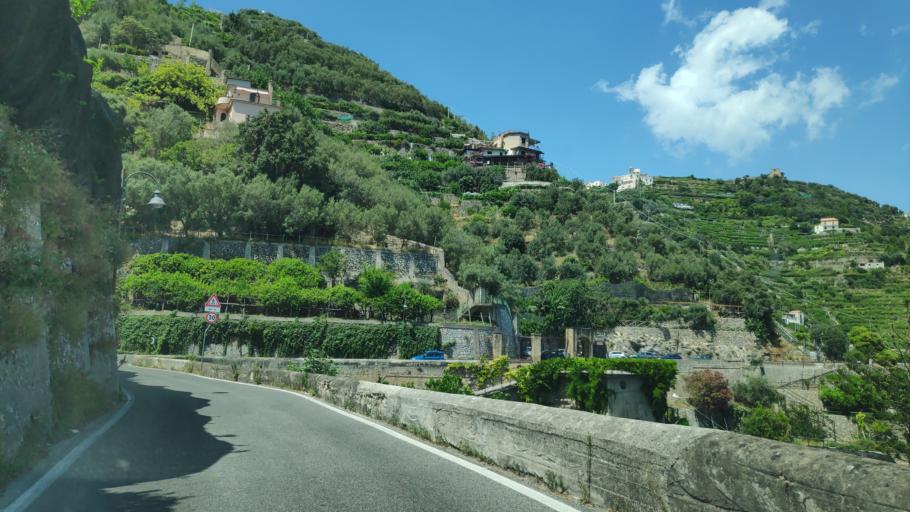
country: IT
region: Campania
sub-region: Provincia di Salerno
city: Ravello
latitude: 40.6430
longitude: 14.6180
